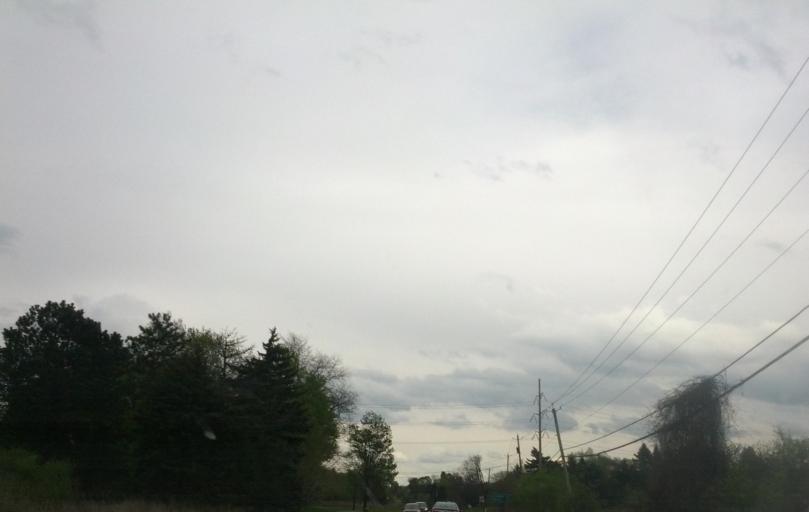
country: US
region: New York
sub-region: Onondaga County
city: Nedrow
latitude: 42.9992
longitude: -76.1245
